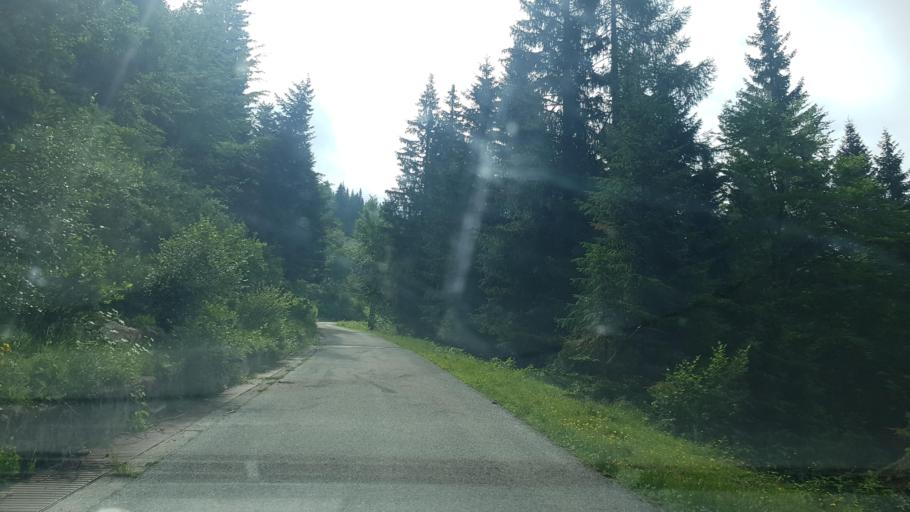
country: IT
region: Friuli Venezia Giulia
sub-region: Provincia di Udine
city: Paularo
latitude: 46.5734
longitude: 13.1613
